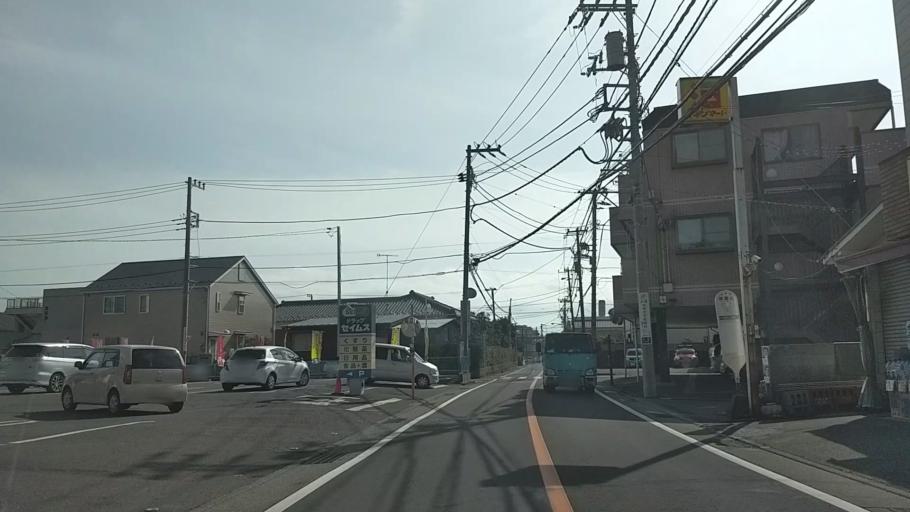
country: JP
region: Kanagawa
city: Chigasaki
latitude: 35.3395
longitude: 139.3829
